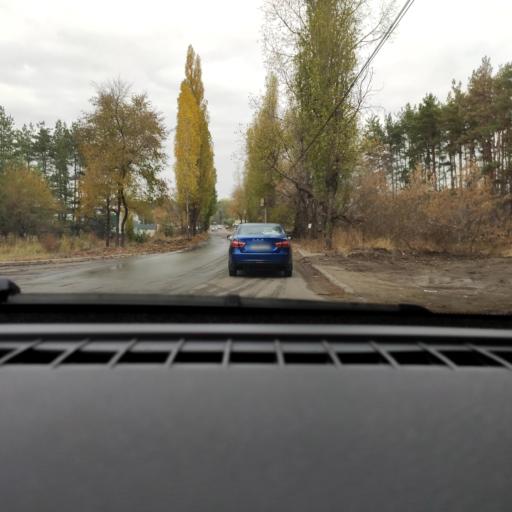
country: RU
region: Voronezj
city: Pridonskoy
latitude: 51.6440
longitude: 39.1092
